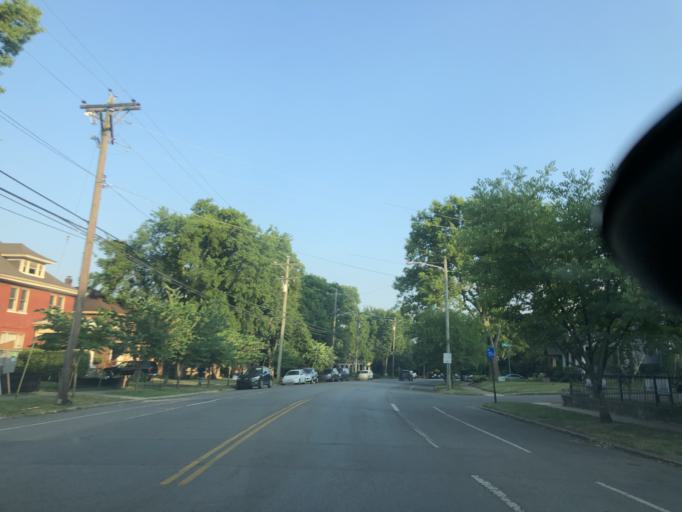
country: US
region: Tennessee
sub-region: Davidson County
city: Nashville
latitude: 36.1278
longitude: -86.7945
